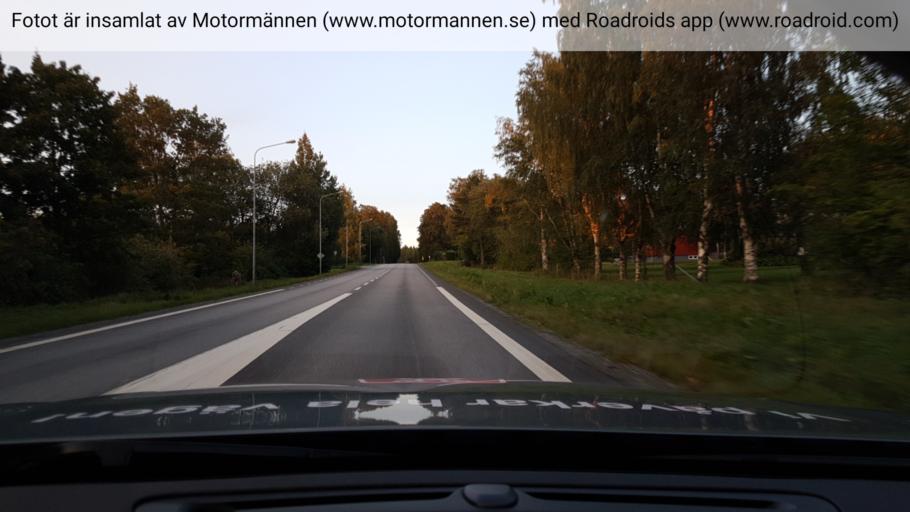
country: SE
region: OErebro
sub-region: Hallefors Kommun
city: Haellefors
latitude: 59.7874
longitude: 14.5346
